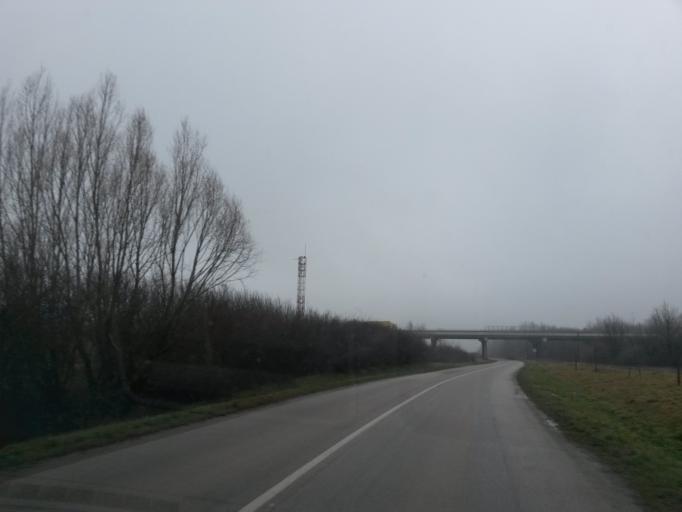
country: HR
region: Vukovarsko-Srijemska
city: Zupanja
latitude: 45.1047
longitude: 18.6990
